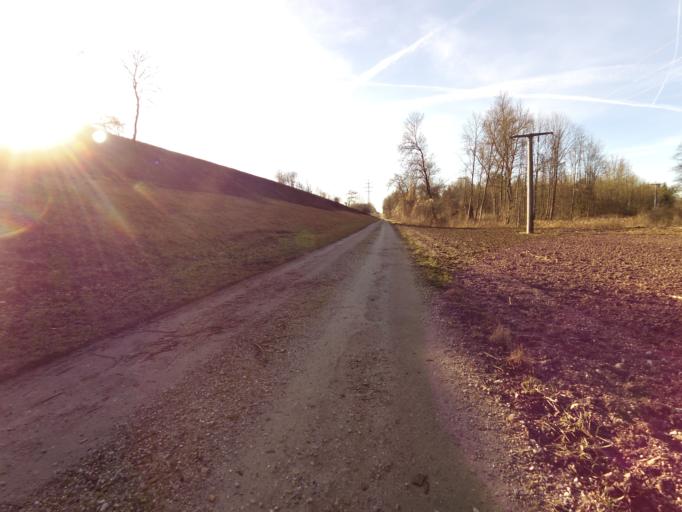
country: DE
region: Bavaria
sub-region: Lower Bavaria
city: Bruckberg
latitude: 48.4927
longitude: 11.9927
